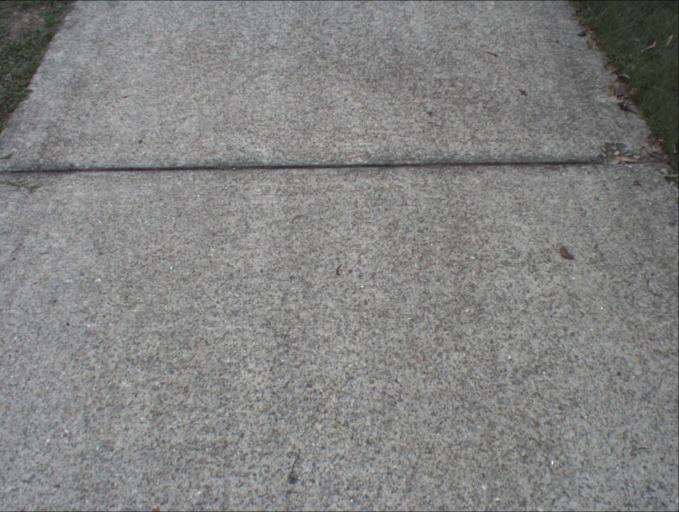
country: AU
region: Queensland
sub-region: Logan
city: Logan Reserve
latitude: -27.6918
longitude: 153.0782
